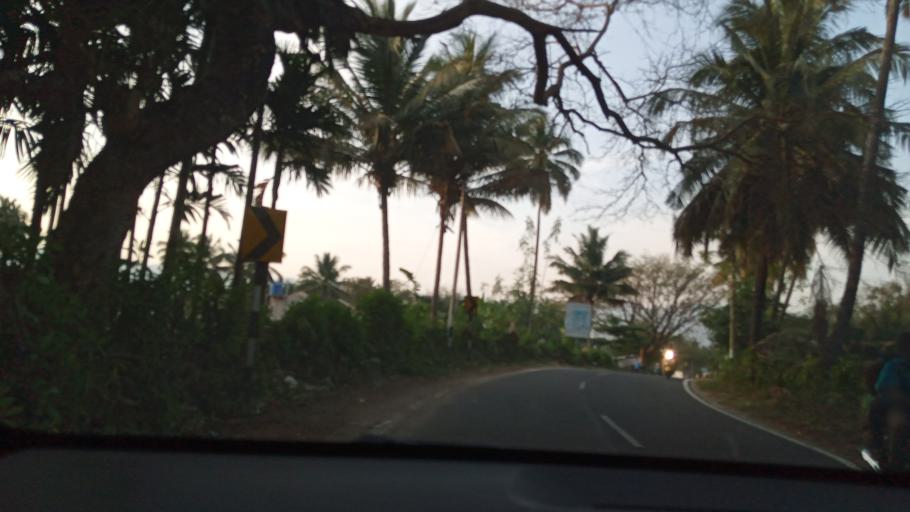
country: IN
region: Tamil Nadu
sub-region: Coimbatore
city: Perur
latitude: 10.9454
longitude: 76.7701
